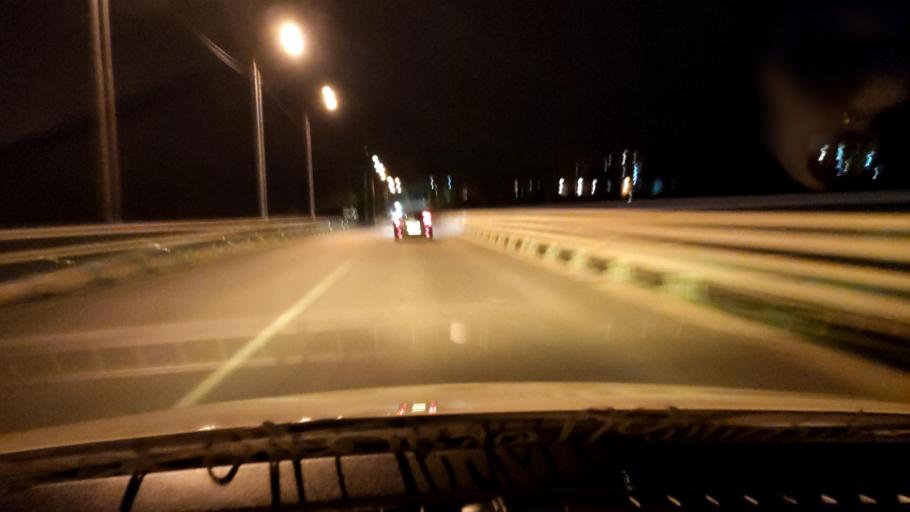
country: RU
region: Voronezj
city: Semiluki
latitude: 51.6748
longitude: 39.0326
